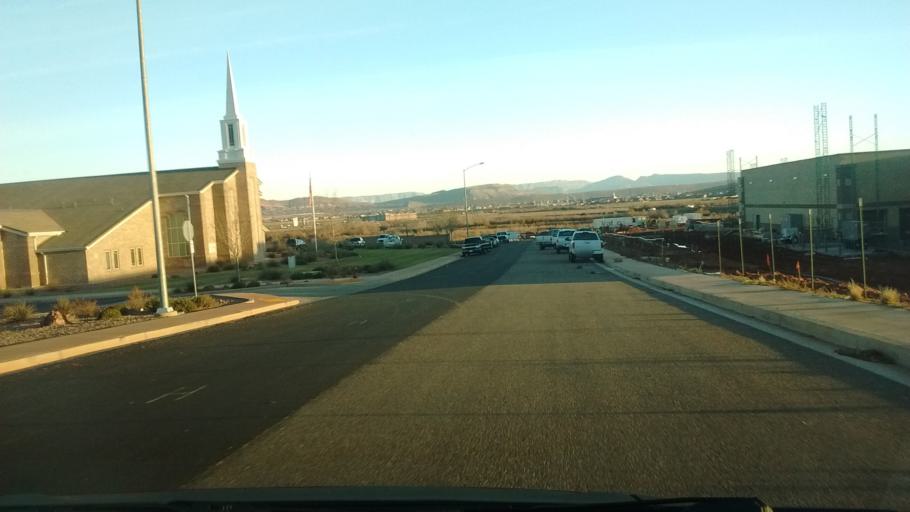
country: US
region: Utah
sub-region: Washington County
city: Washington
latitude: 37.1010
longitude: -113.5338
